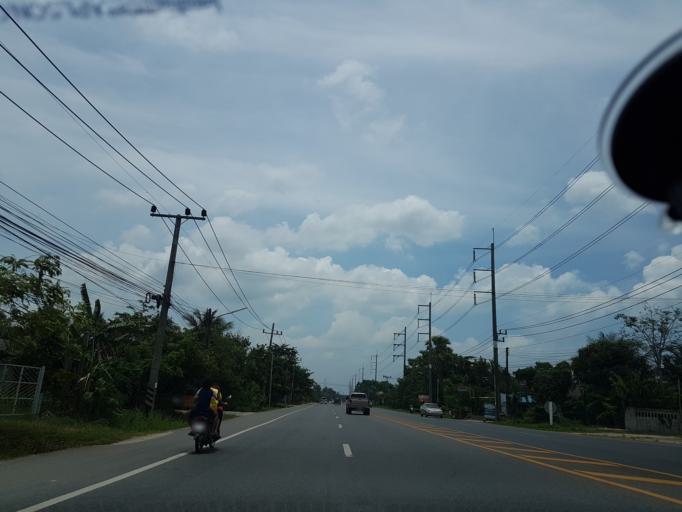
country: TH
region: Songkhla
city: Songkhla
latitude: 7.1258
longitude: 100.6318
